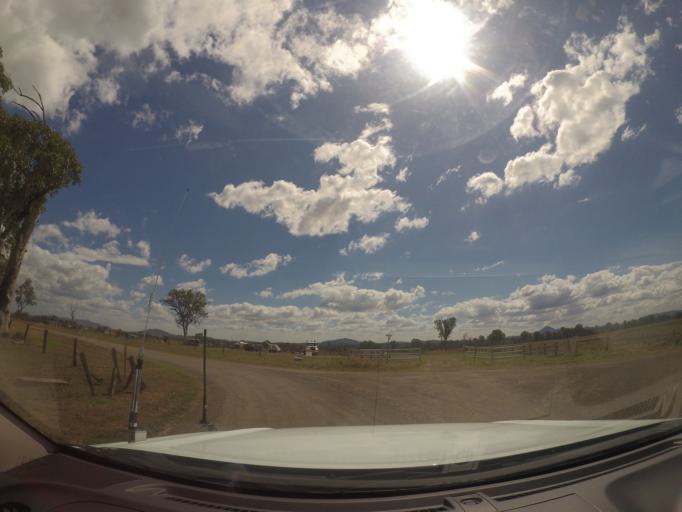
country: AU
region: Queensland
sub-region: Logan
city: Cedar Vale
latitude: -27.8924
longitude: 152.9593
